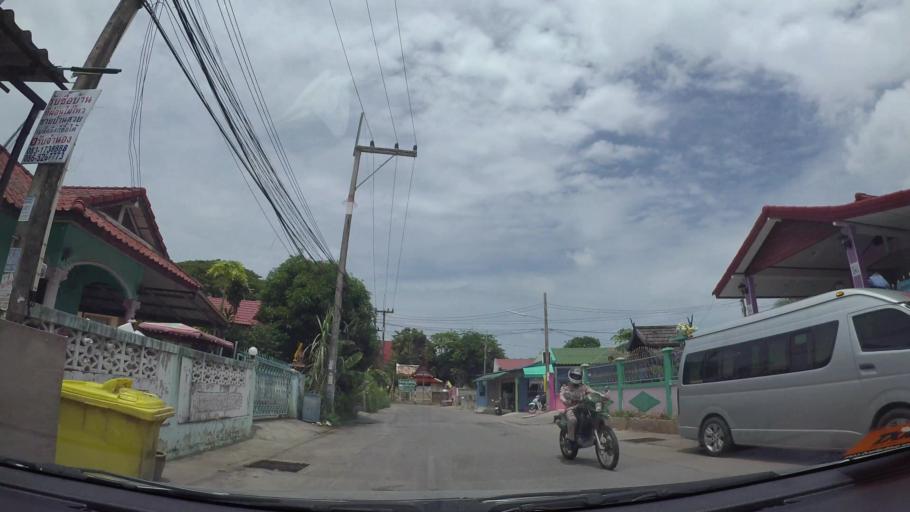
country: TH
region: Chon Buri
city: Sattahip
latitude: 12.6820
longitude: 100.9021
